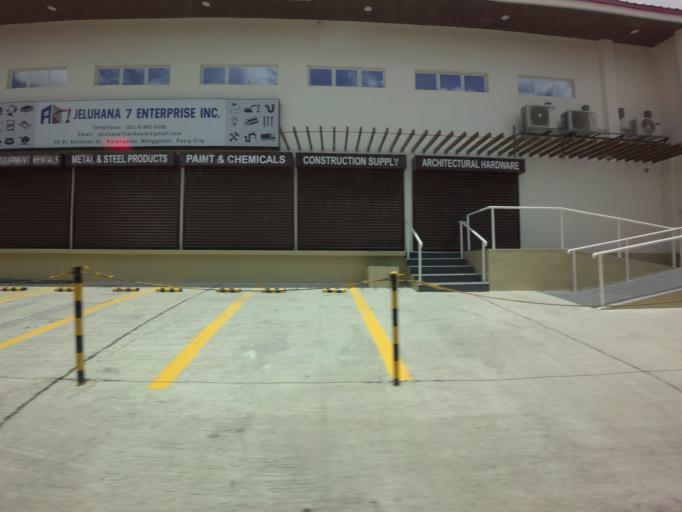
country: PH
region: Metro Manila
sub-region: Marikina
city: Calumpang
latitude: 14.6071
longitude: 121.1038
